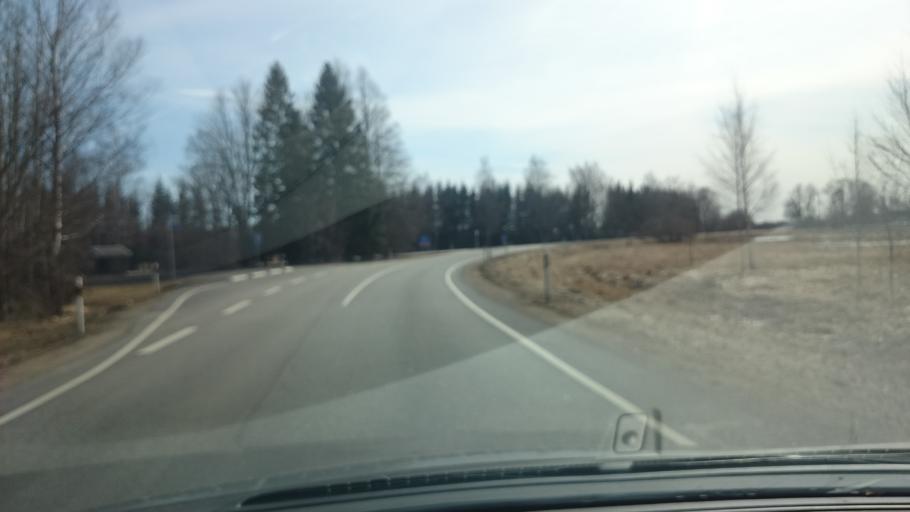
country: EE
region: Paernumaa
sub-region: Vaendra vald (alev)
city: Vandra
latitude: 58.6271
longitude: 24.9230
